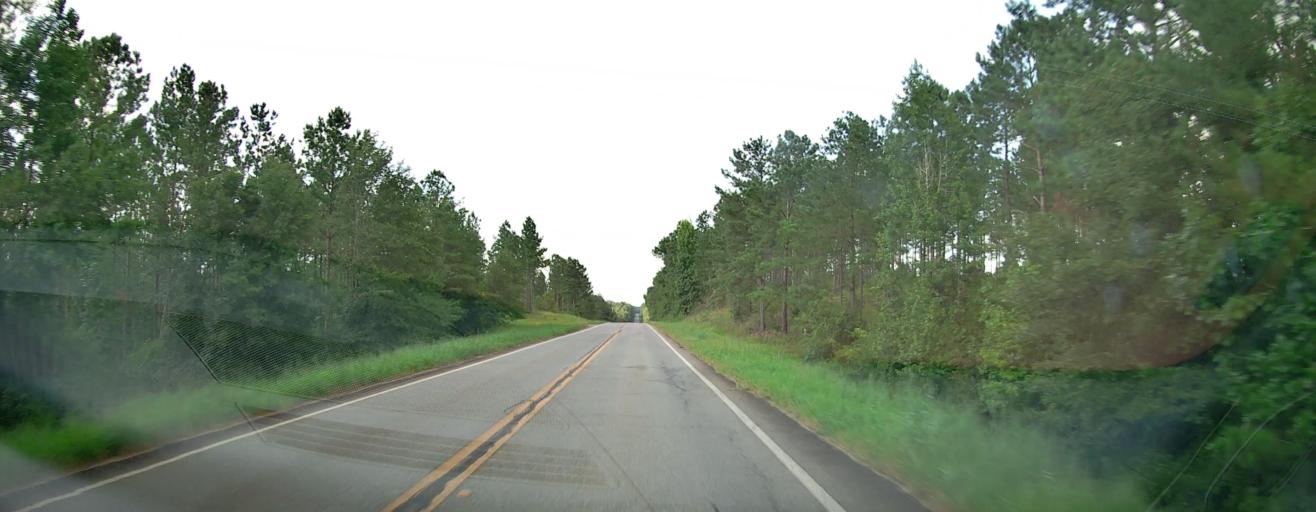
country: US
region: Georgia
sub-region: Crawford County
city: Roberta
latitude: 32.8171
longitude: -84.0233
